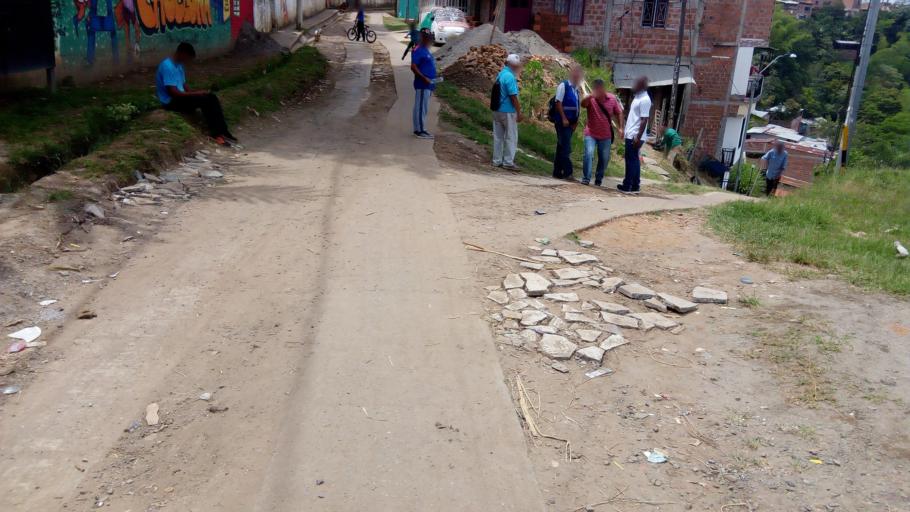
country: CO
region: Valle del Cauca
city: Cali
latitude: 3.3831
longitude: -76.5639
